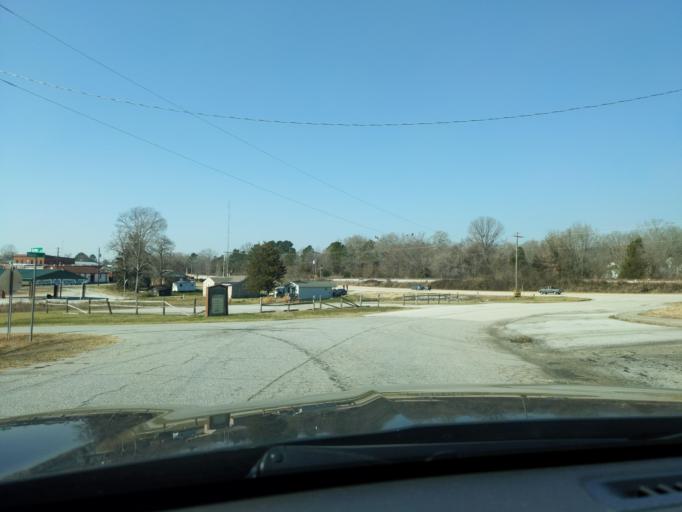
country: US
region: South Carolina
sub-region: Abbeville County
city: Calhoun Falls
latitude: 34.0931
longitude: -82.5928
